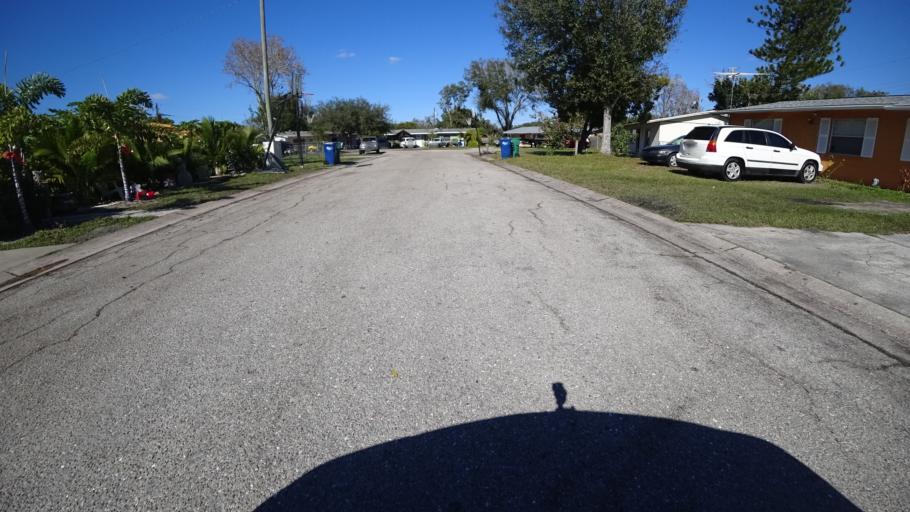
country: US
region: Florida
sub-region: Manatee County
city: Whitfield
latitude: 27.4331
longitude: -82.5516
